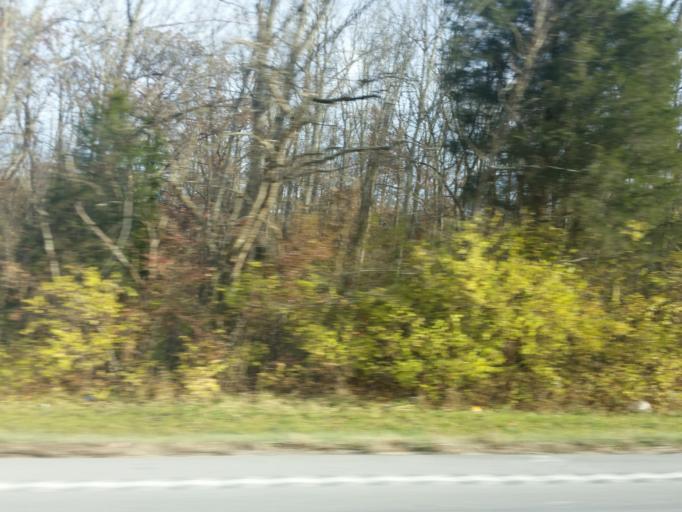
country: US
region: Kentucky
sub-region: Pendleton County
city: Falmouth
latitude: 38.7317
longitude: -84.3719
